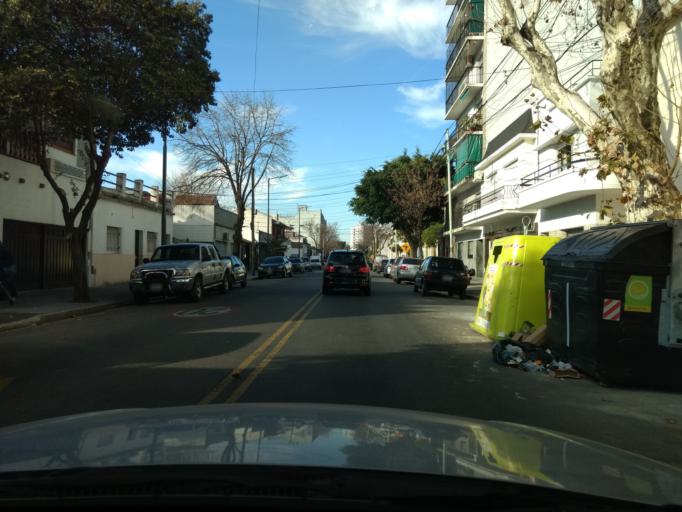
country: AR
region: Buenos Aires F.D.
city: Villa Santa Rita
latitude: -34.6345
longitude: -58.4950
